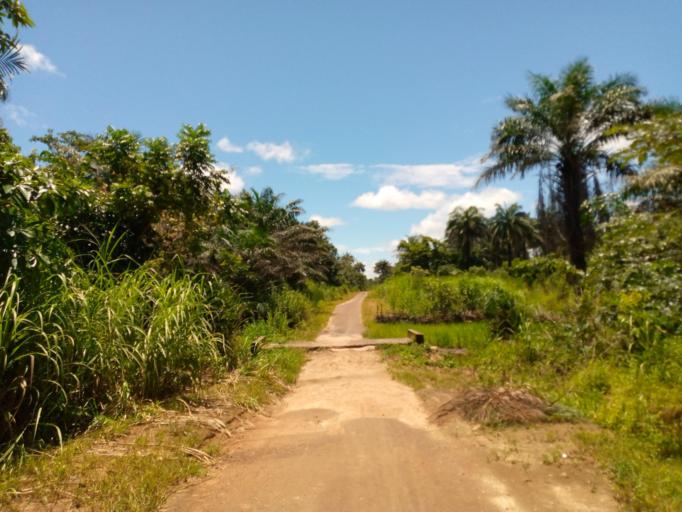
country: SL
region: Northern Province
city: Binkolo
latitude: 9.0950
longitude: -12.1421
